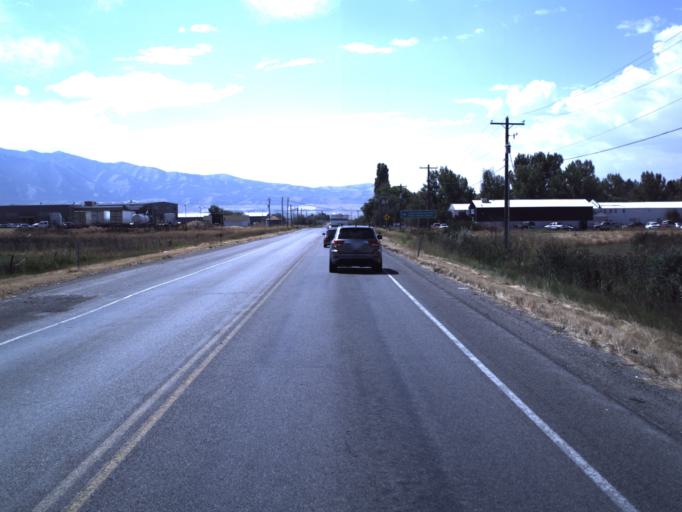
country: US
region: Utah
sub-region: Cache County
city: Logan
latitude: 41.7358
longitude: -111.8660
